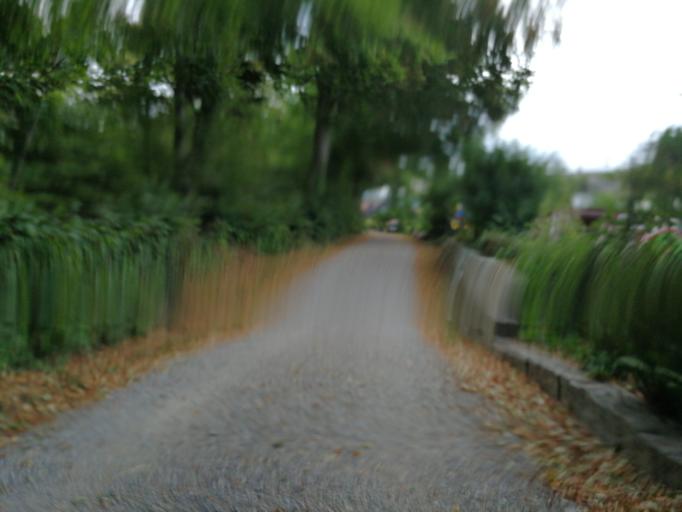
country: CH
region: Zurich
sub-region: Bezirk Hinwil
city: Wetzikon / Robenhausen
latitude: 47.3339
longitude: 8.7634
